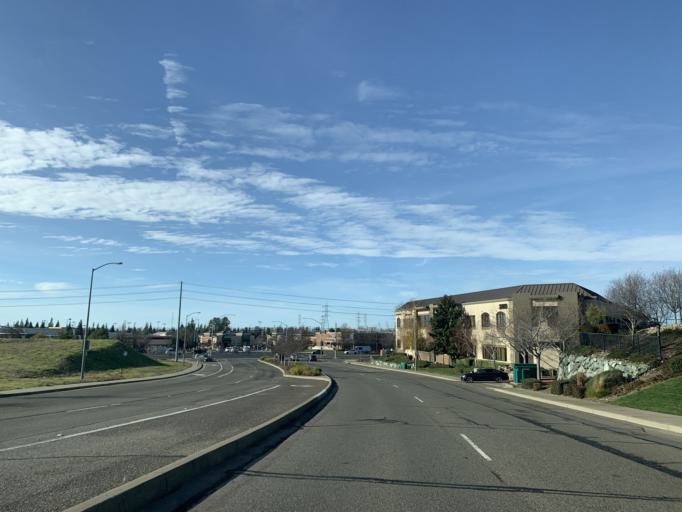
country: US
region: California
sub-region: El Dorado County
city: El Dorado Hills
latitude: 38.6593
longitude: -121.1269
